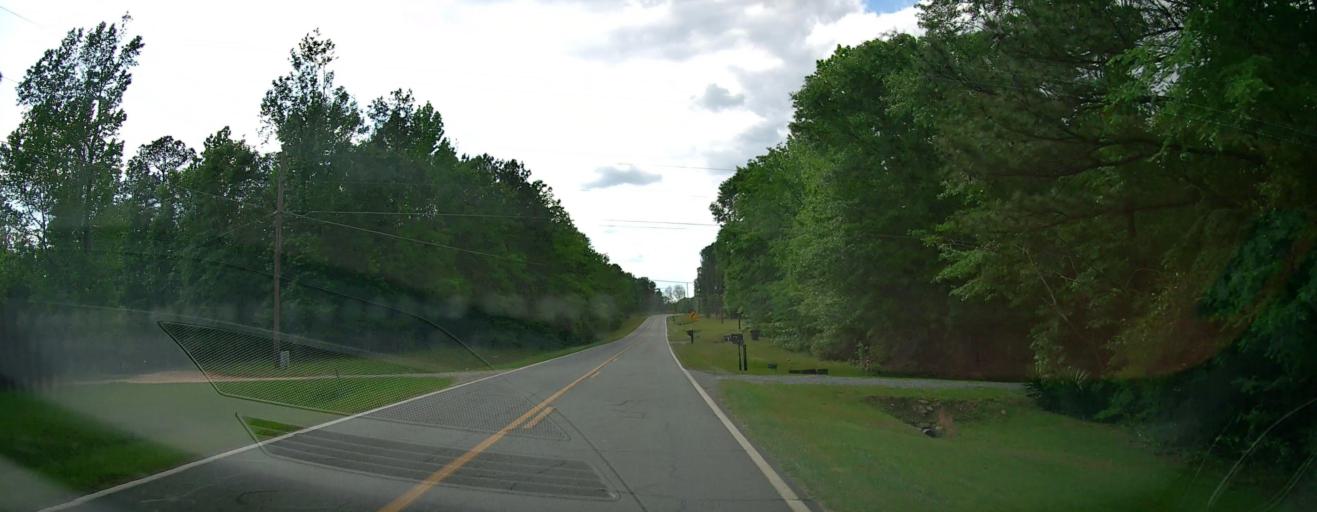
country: US
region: Georgia
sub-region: Baldwin County
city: Hardwick
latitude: 33.0644
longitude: -83.1691
